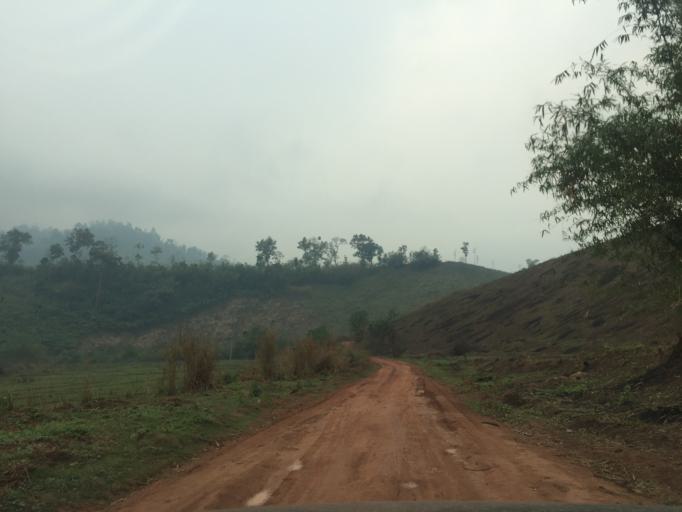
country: TH
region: Nan
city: Bo Kluea
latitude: 18.8482
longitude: 101.4175
